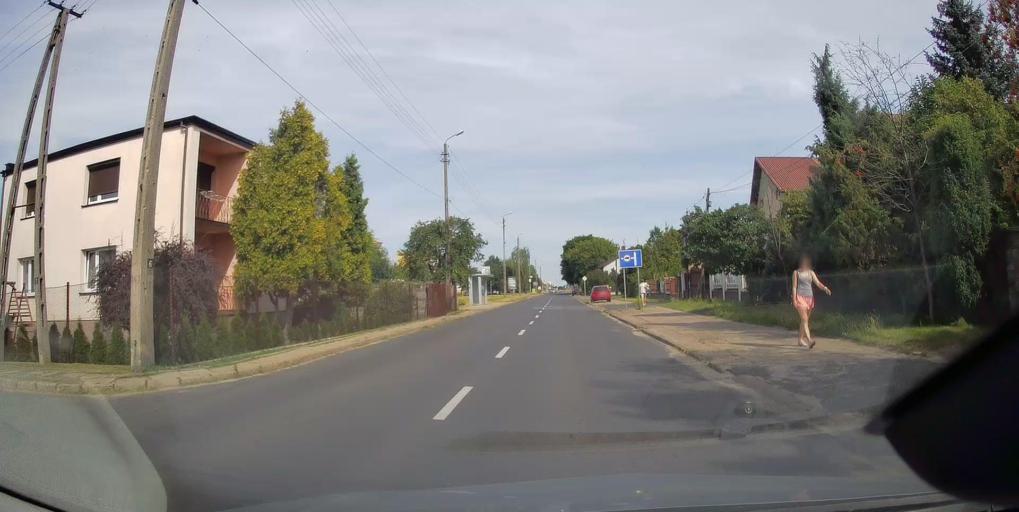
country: PL
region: Lodz Voivodeship
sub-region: Powiat tomaszowski
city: Tomaszow Mazowiecki
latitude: 51.5214
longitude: 19.9979
